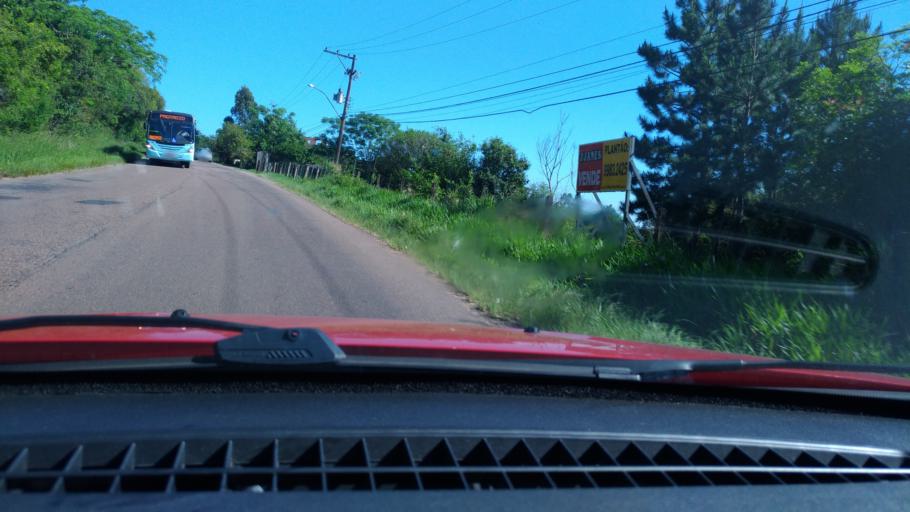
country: BR
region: Rio Grande do Sul
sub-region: Viamao
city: Viamao
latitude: -30.0664
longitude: -51.0532
